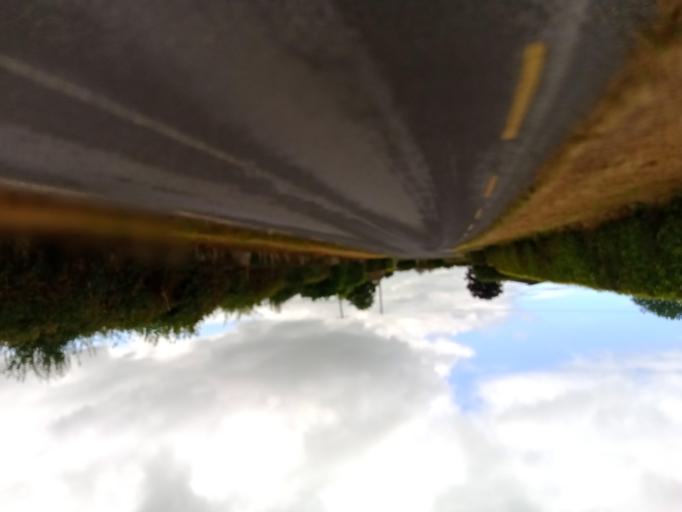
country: IE
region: Leinster
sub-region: Kilkenny
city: Callan
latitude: 52.5736
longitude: -7.4047
